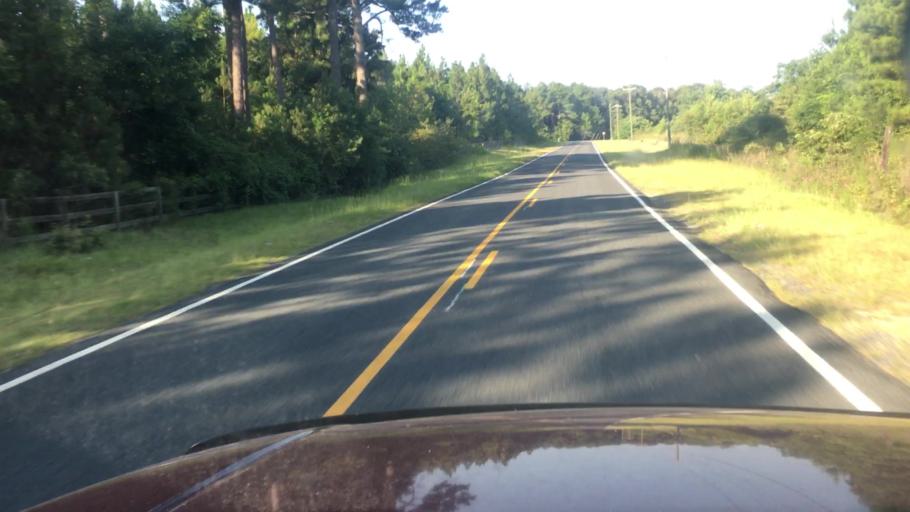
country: US
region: North Carolina
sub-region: Robeson County
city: Saint Pauls
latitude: 34.8502
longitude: -78.8574
